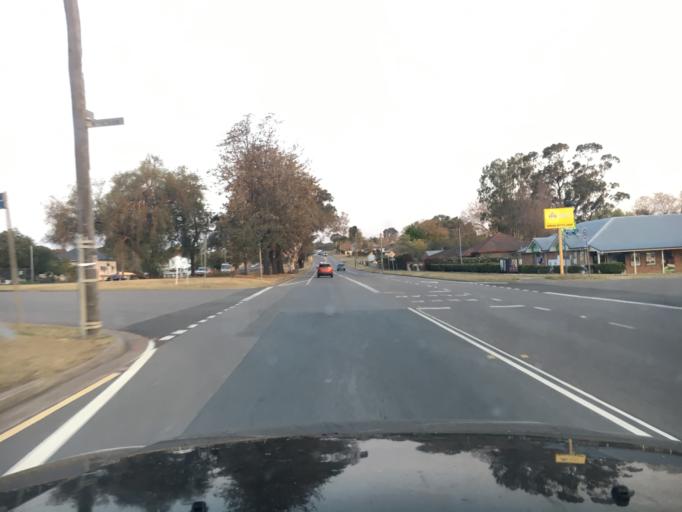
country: AU
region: New South Wales
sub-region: Cessnock
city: Greta
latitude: -32.6788
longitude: 151.3899
